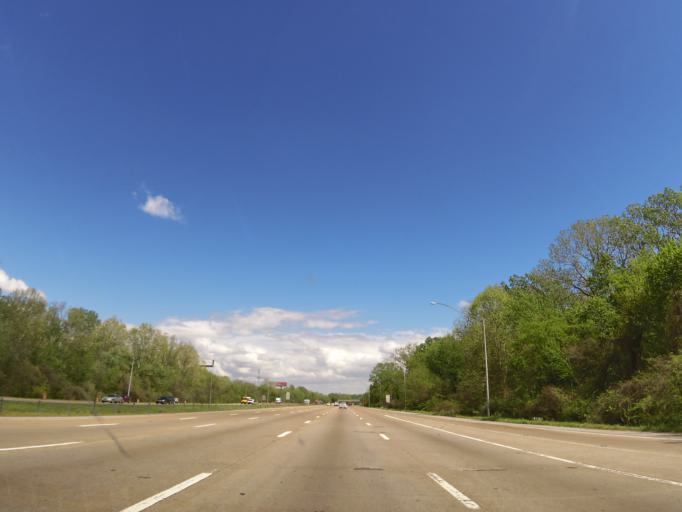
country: US
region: Tennessee
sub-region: Shelby County
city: Memphis
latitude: 35.1921
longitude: -90.0035
